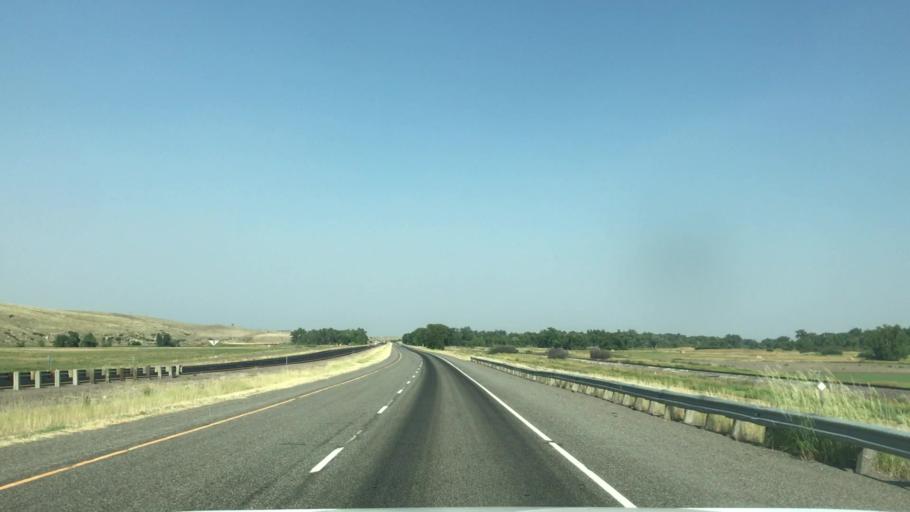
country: US
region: Montana
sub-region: Cascade County
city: Sun Prairie
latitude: 47.2309
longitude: -111.7556
